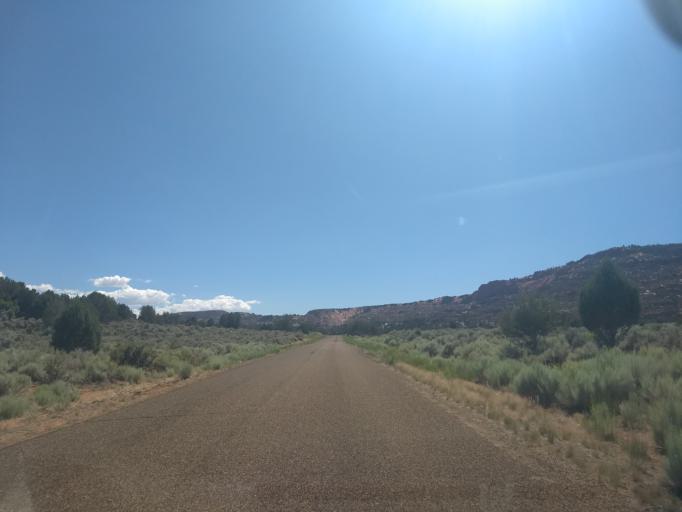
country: US
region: Utah
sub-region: Washington County
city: Hildale
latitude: 37.0084
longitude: -112.8517
